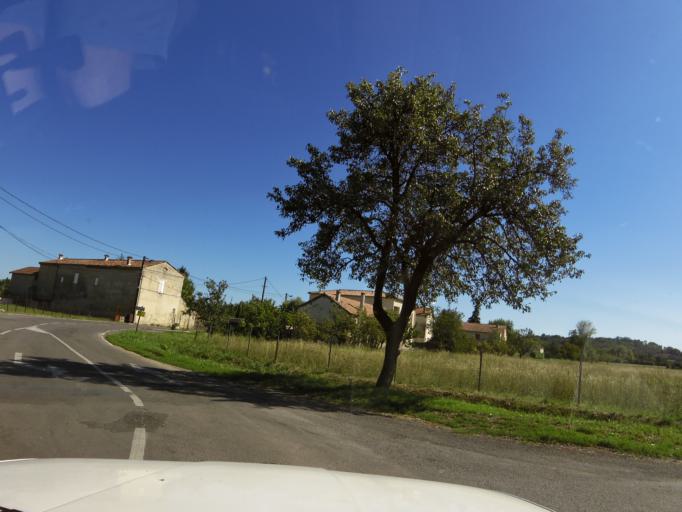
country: FR
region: Languedoc-Roussillon
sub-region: Departement du Gard
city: Ales
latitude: 44.1121
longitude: 4.0854
